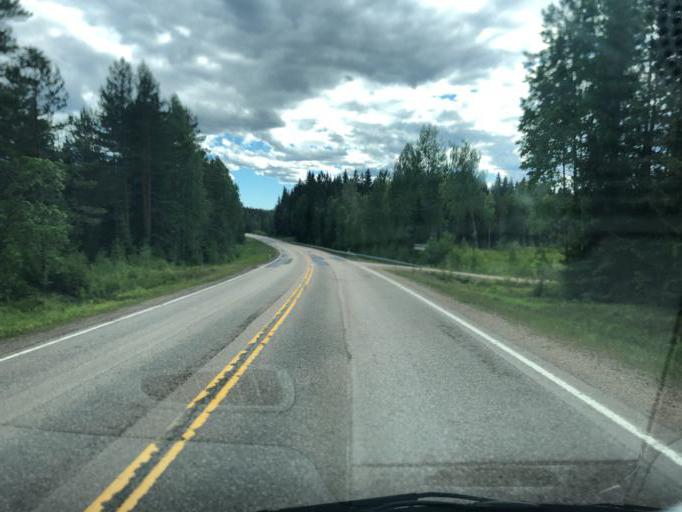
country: FI
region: Southern Savonia
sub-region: Mikkeli
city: Maentyharju
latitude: 61.1388
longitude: 27.1049
